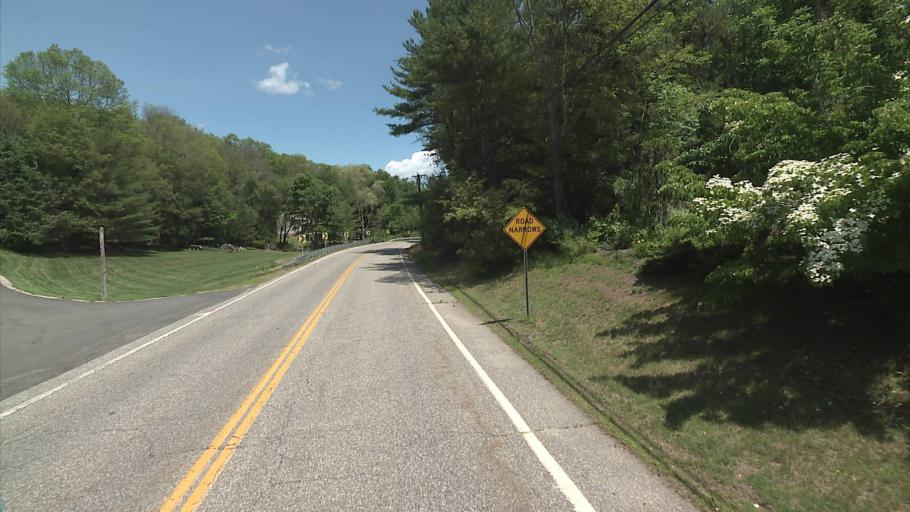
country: US
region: Connecticut
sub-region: New London County
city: Preston City
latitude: 41.5174
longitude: -71.8900
